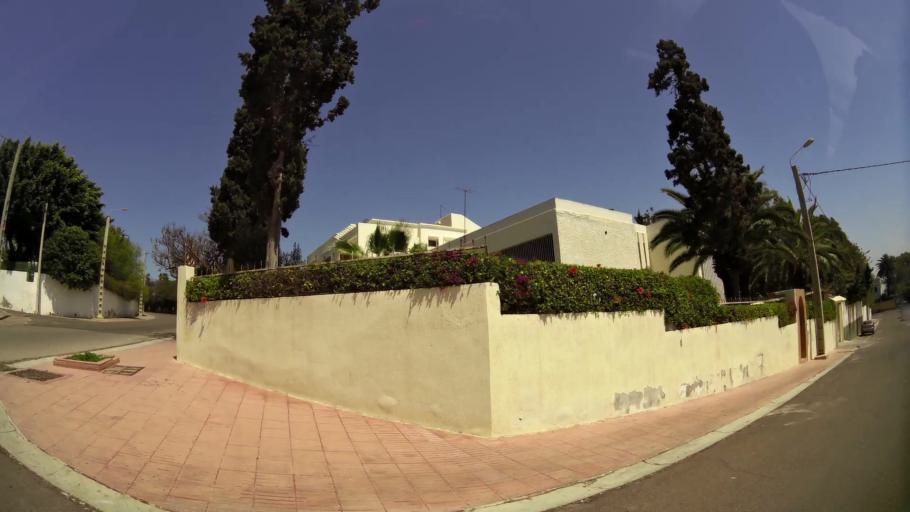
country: MA
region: Souss-Massa-Draa
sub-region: Agadir-Ida-ou-Tnan
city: Agadir
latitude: 30.4265
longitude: -9.5980
